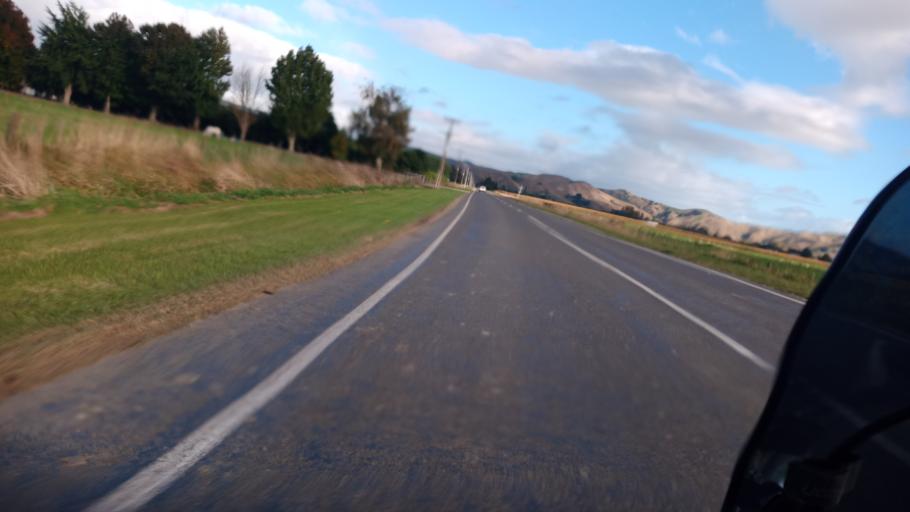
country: NZ
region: Gisborne
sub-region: Gisborne District
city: Gisborne
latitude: -38.6340
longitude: 177.9053
